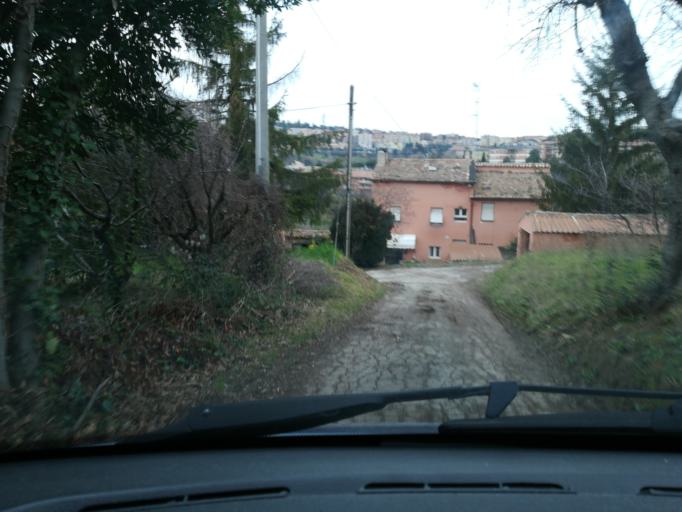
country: IT
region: The Marches
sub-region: Provincia di Macerata
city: Macerata
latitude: 43.2896
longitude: 13.4477
